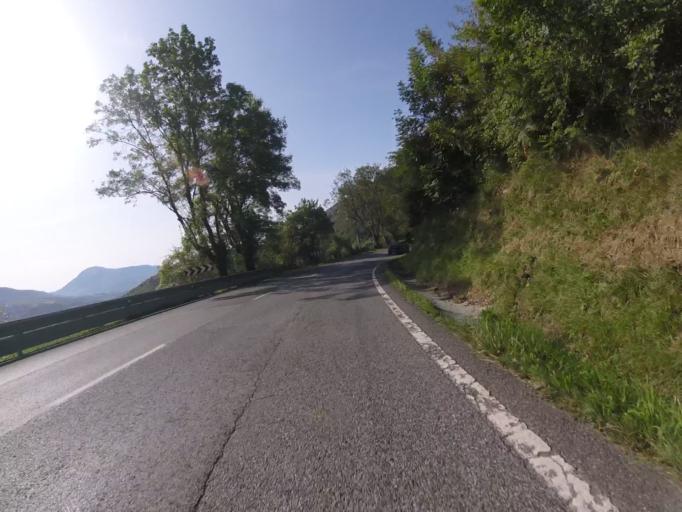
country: ES
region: Navarre
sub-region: Provincia de Navarra
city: Zugarramurdi
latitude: 43.2298
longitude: -1.4972
